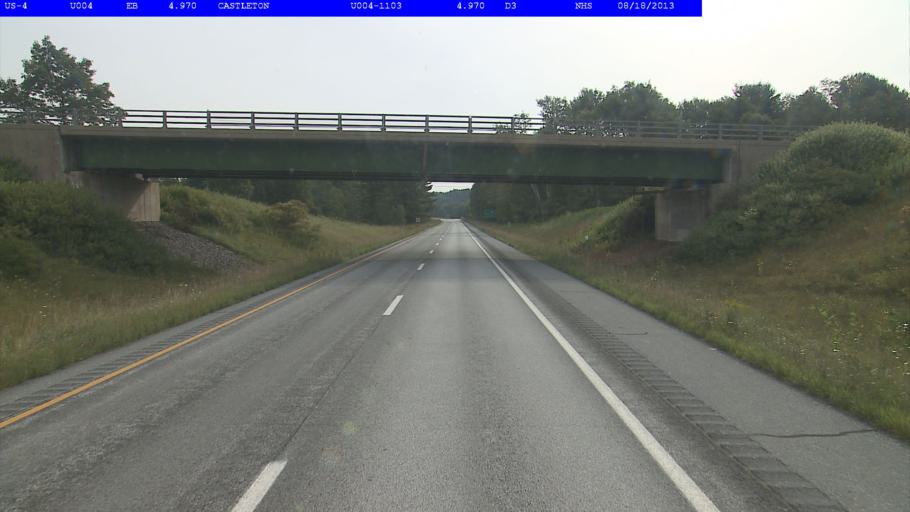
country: US
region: Vermont
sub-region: Rutland County
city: Castleton
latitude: 43.6140
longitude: -73.2157
